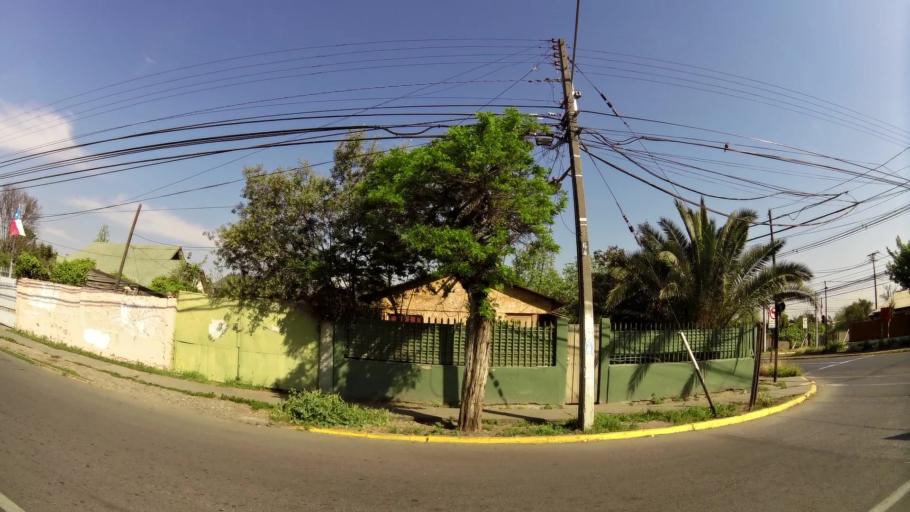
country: CL
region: Santiago Metropolitan
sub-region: Provincia de Santiago
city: La Pintana
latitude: -33.5472
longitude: -70.5936
